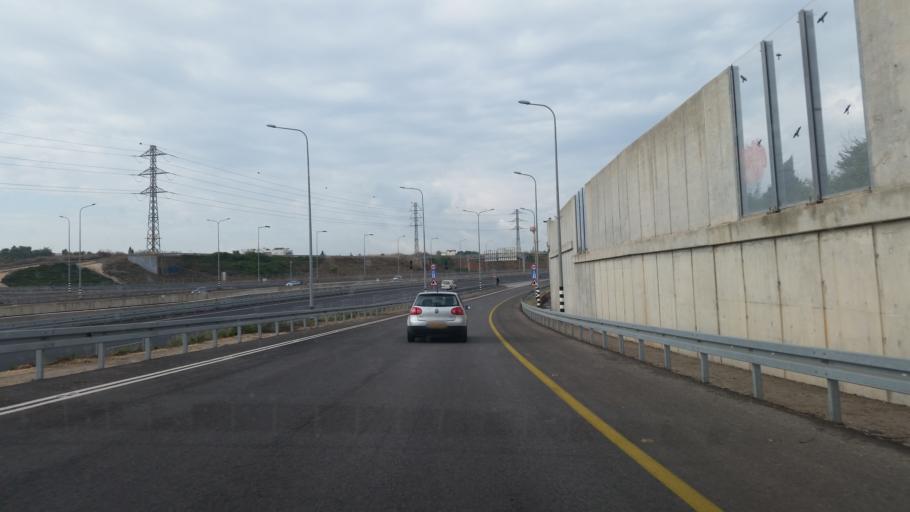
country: IL
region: Central District
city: Ra'anana
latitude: 32.1724
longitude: 34.8669
